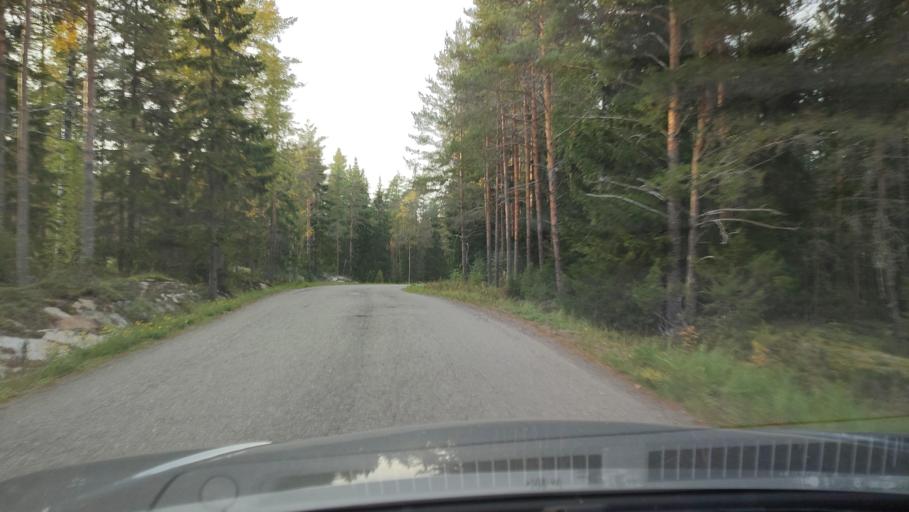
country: FI
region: Southern Ostrobothnia
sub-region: Suupohja
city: Karijoki
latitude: 62.1313
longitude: 21.5773
